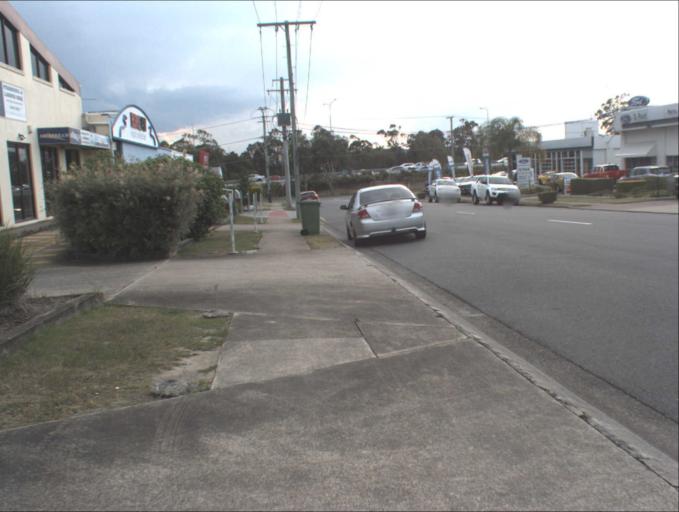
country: AU
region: Queensland
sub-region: Logan
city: Springwood
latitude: -27.6169
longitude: 153.1267
